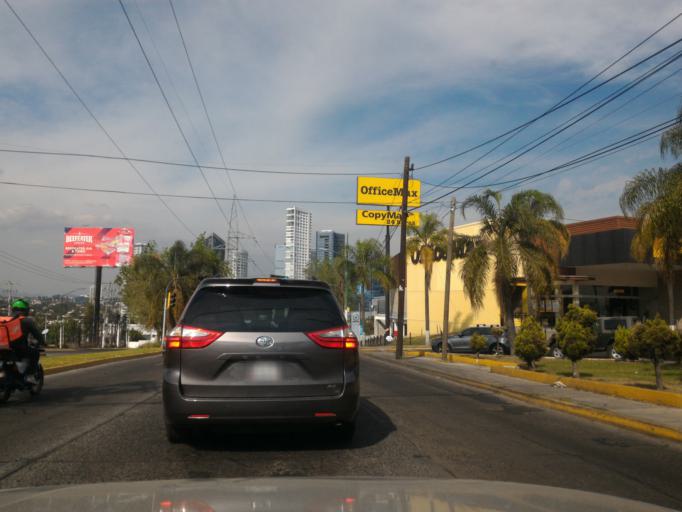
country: MX
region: Jalisco
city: Zapopan2
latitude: 20.7003
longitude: -103.4156
